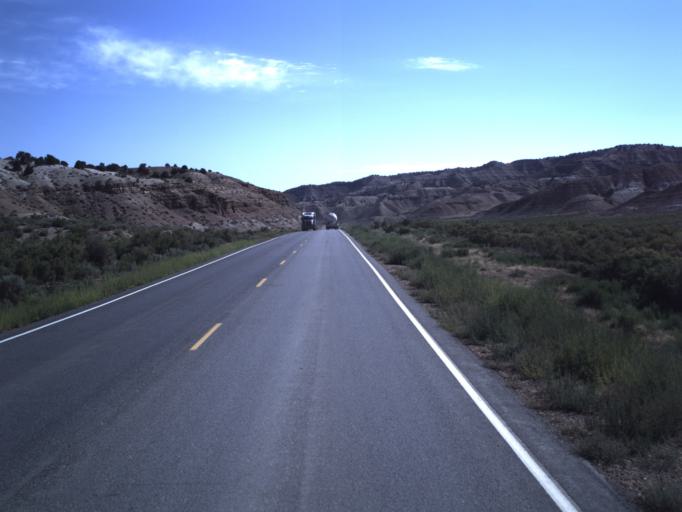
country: US
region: Utah
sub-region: Duchesne County
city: Duchesne
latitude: 40.1276
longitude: -110.4388
